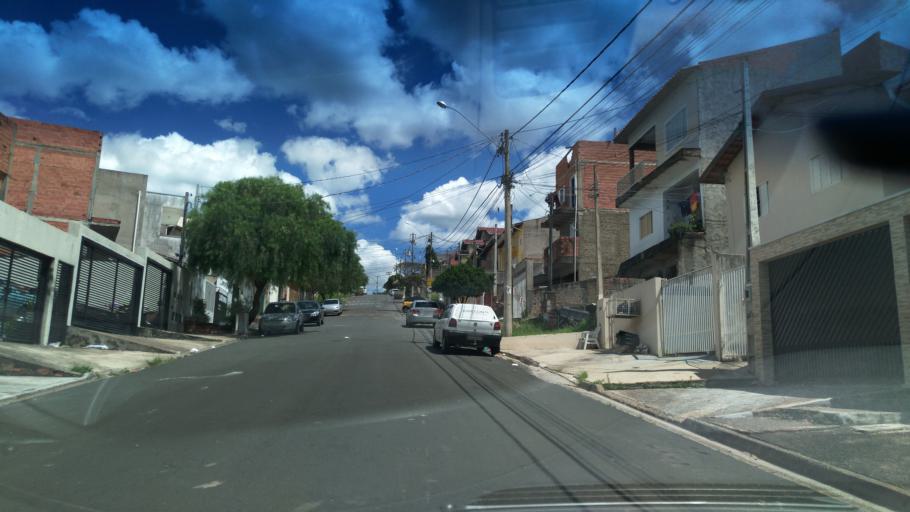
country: BR
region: Sao Paulo
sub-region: Valinhos
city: Valinhos
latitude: -22.9529
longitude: -47.0075
